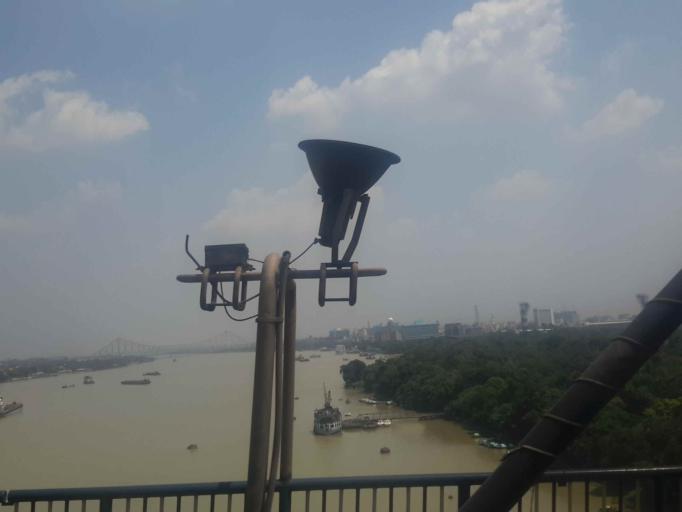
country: IN
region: West Bengal
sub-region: Kolkata
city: Bara Bazar
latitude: 22.5559
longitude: 88.3294
